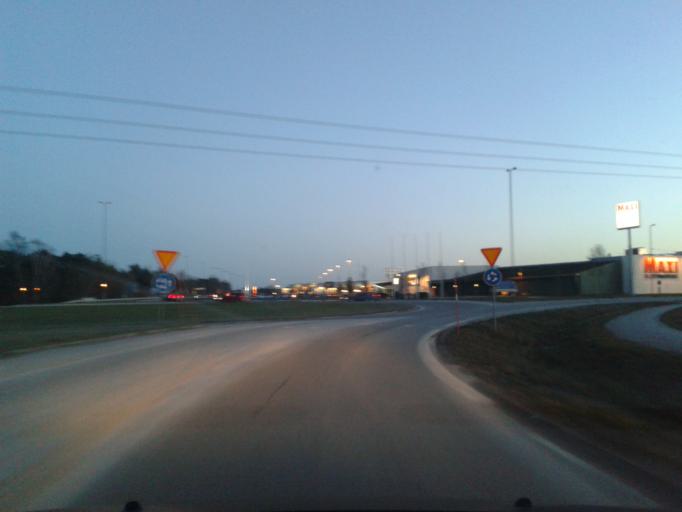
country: SE
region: Gotland
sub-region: Gotland
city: Visby
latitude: 57.6254
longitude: 18.3205
